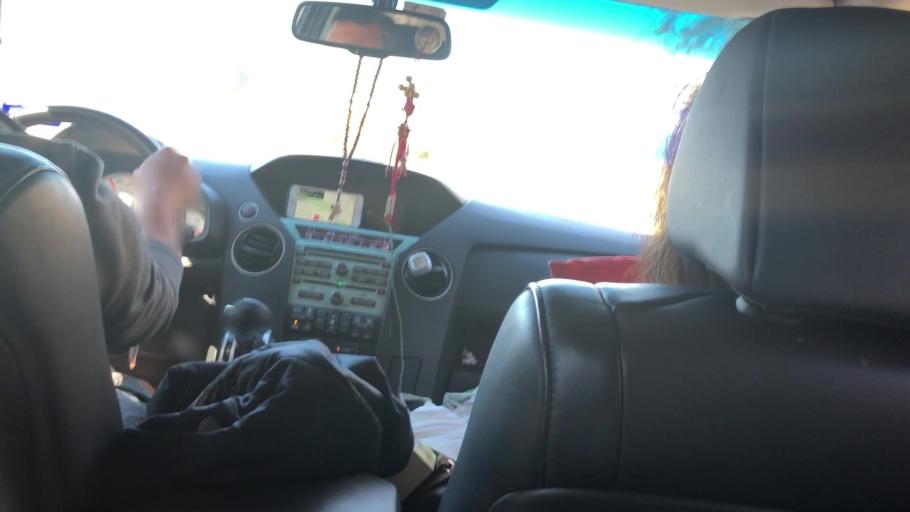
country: US
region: Louisiana
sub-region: Saint John the Baptist Parish
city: Montegut
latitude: 30.1040
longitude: -90.4920
